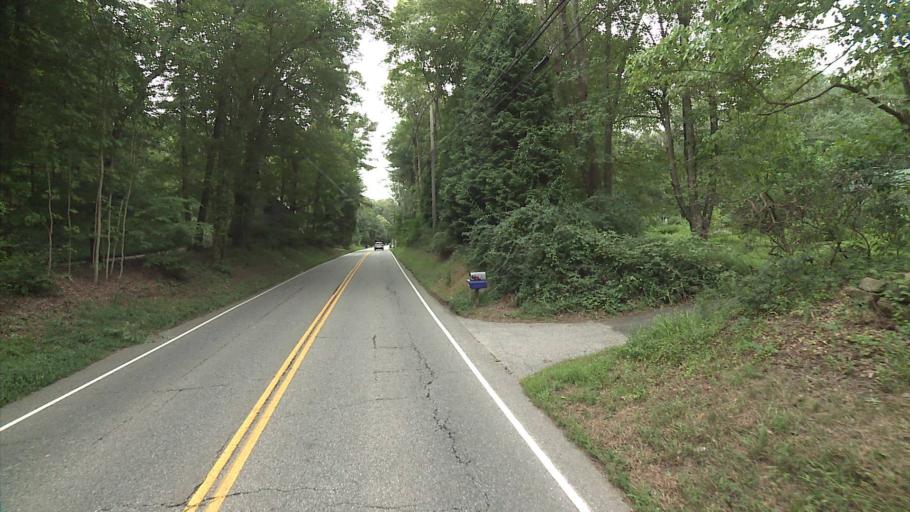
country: US
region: Connecticut
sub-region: Middlesex County
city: Old Saybrook Center
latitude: 41.3351
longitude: -72.3378
